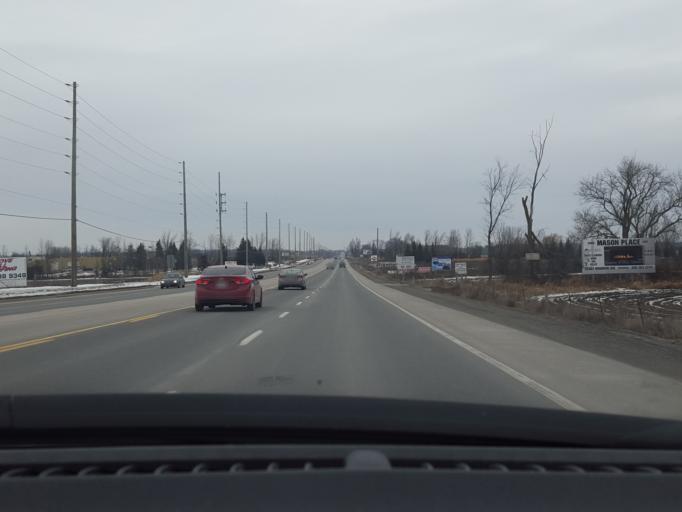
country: CA
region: Ontario
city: Keswick
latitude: 44.2087
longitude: -79.4422
